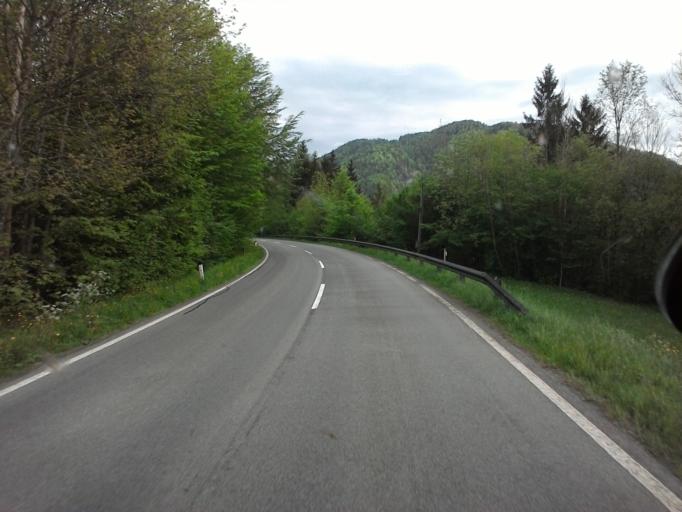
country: AT
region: Styria
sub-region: Politischer Bezirk Liezen
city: Altenmarkt bei Sankt Gallen
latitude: 47.7133
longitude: 14.6792
